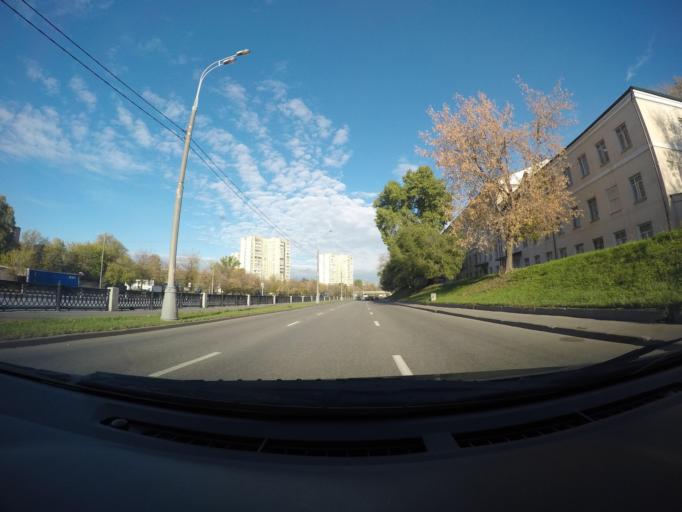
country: RU
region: Moskovskaya
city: Bogorodskoye
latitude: 55.7979
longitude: 37.7008
